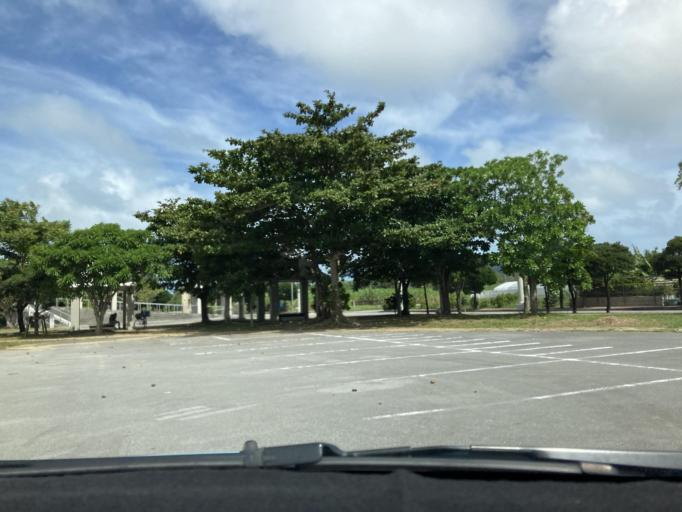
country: JP
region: Okinawa
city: Ginowan
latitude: 26.1693
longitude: 127.7878
